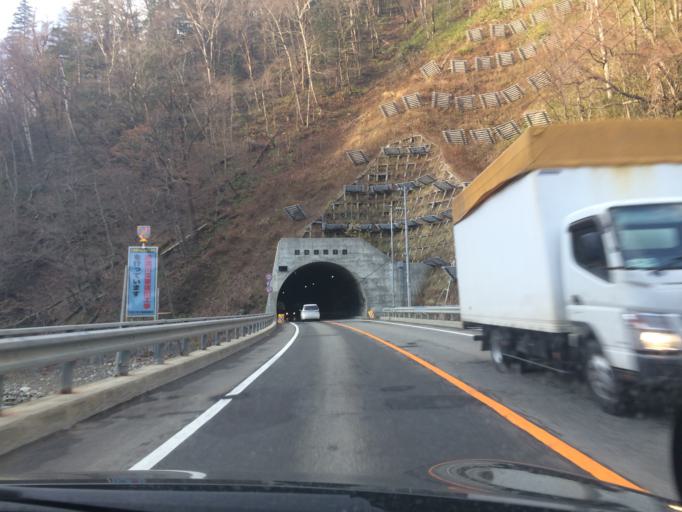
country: JP
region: Hokkaido
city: Shimo-furano
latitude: 42.9609
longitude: 142.6173
